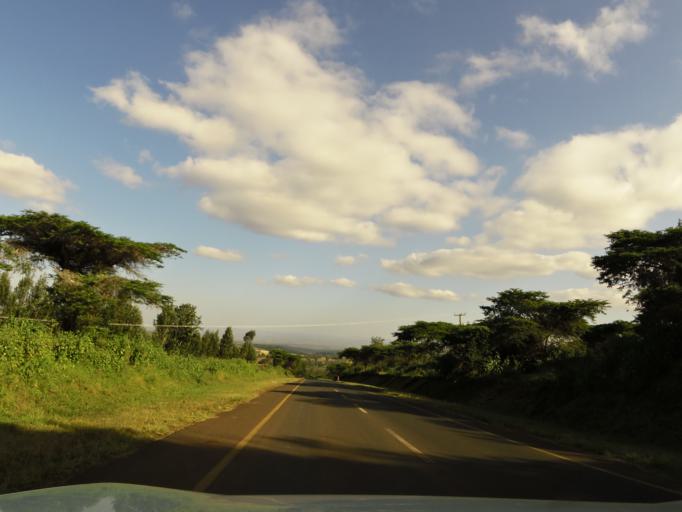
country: TZ
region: Arusha
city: Kiratu
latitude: -3.3057
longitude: 35.5915
